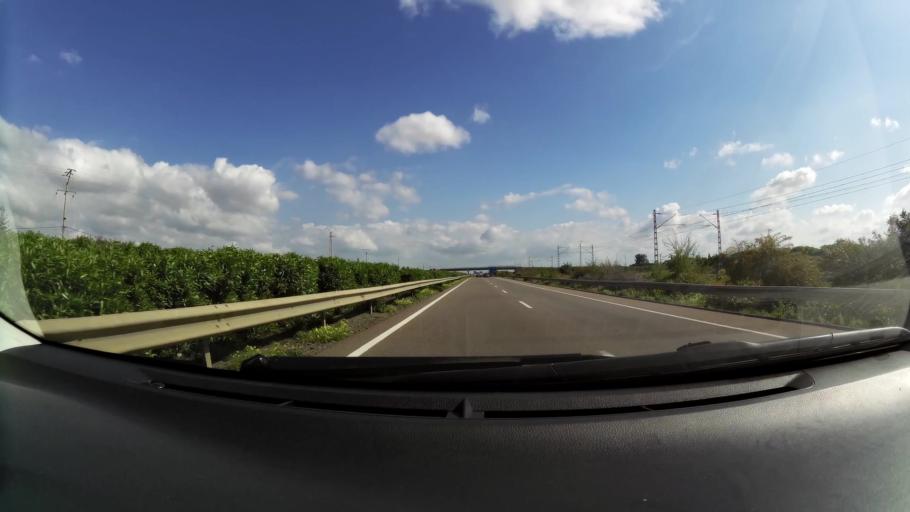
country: MA
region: Chaouia-Ouardigha
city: Nouaseur
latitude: 33.3366
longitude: -7.6109
